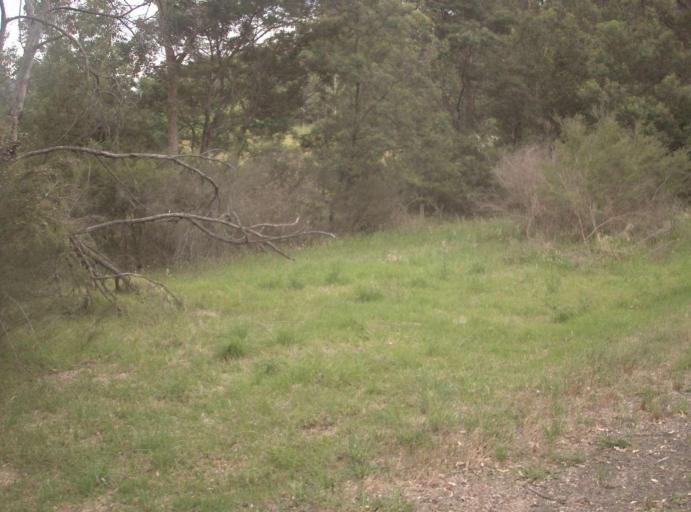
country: AU
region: Victoria
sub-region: East Gippsland
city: Bairnsdale
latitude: -37.7431
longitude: 147.5989
